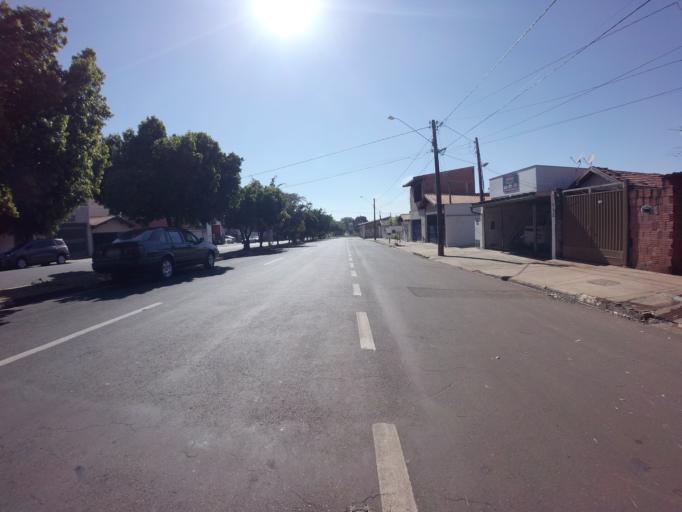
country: BR
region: Sao Paulo
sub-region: Piracicaba
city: Piracicaba
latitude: -22.7695
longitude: -47.5874
